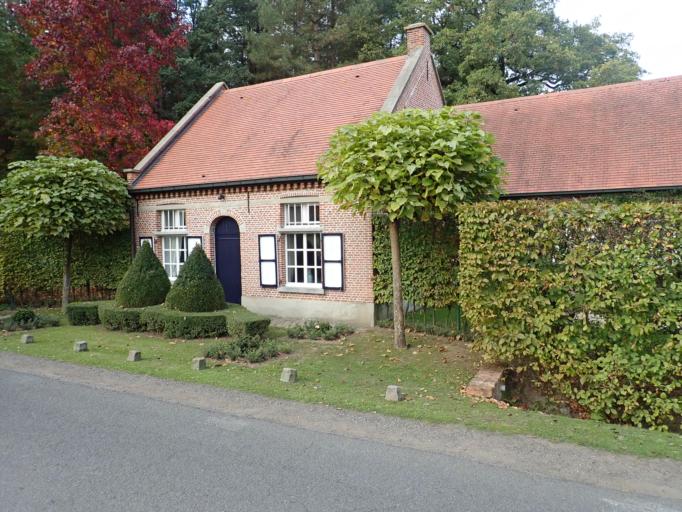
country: BE
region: Flanders
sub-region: Provincie Antwerpen
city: Berlaar
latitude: 51.1212
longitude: 4.6887
